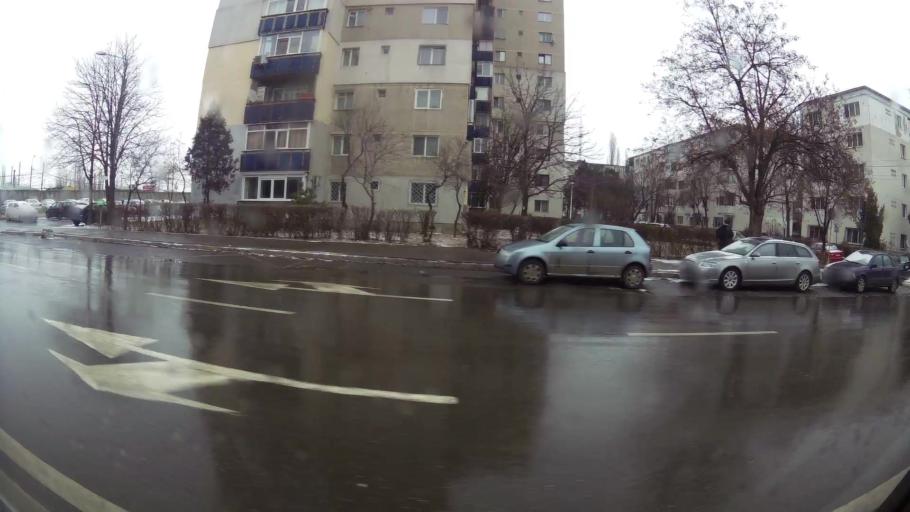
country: RO
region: Prahova
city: Ploiesti
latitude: 44.9578
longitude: 26.0127
